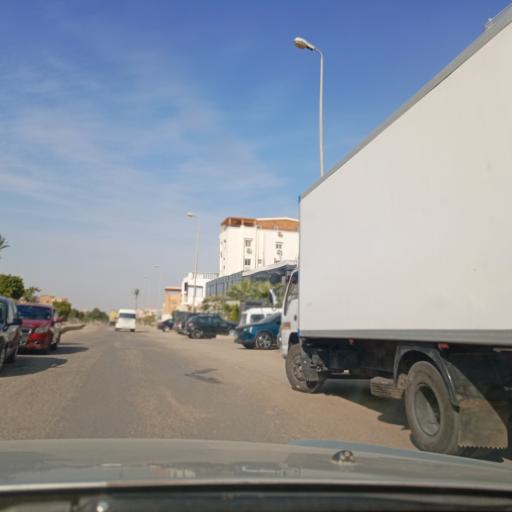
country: EG
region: Muhafazat al Qalyubiyah
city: Al Khankah
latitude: 30.0353
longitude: 31.4855
